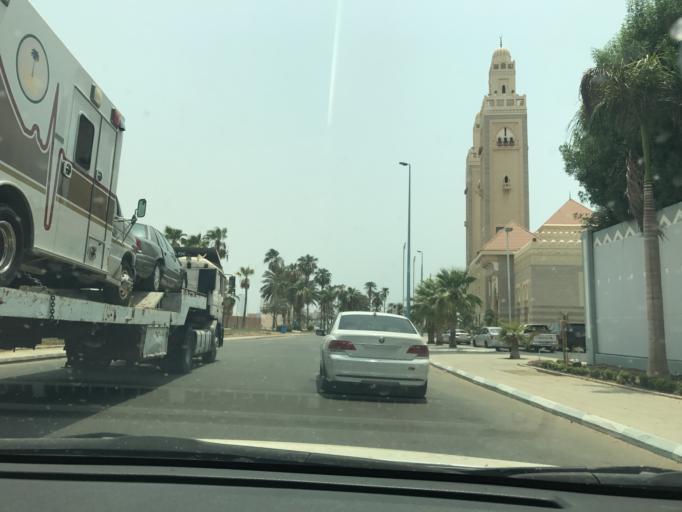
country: SA
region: Makkah
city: Jeddah
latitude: 21.6683
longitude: 39.1039
